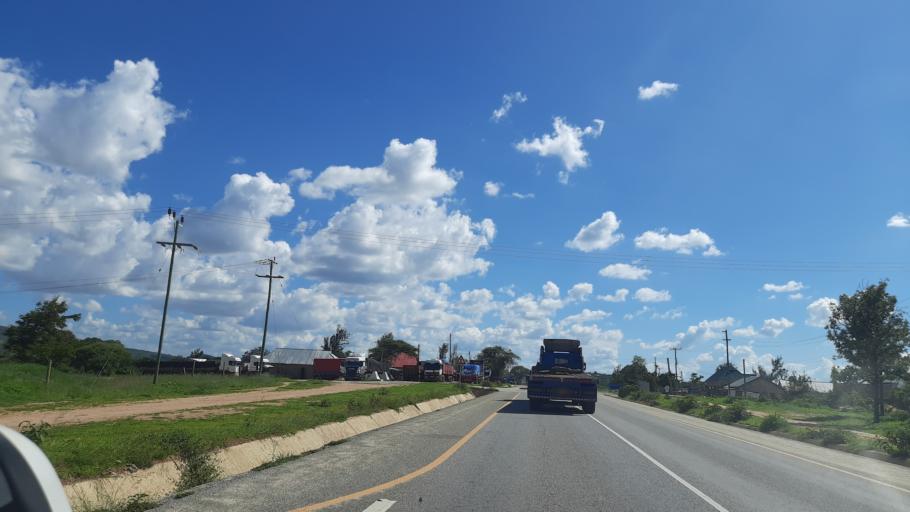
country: TZ
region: Dodoma
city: Kondoa
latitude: -4.9151
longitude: 35.8106
